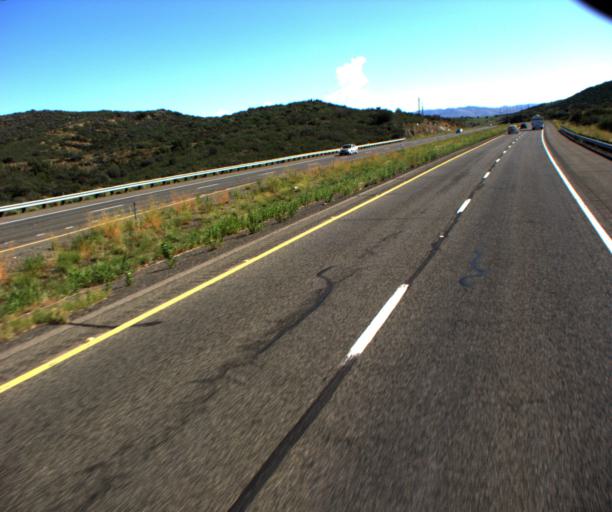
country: US
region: Arizona
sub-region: Yavapai County
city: Dewey-Humboldt
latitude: 34.4840
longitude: -112.2559
